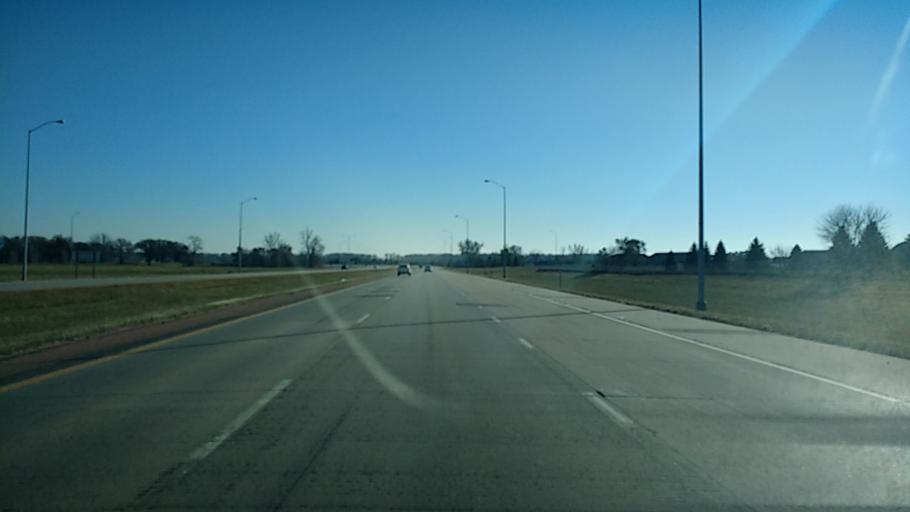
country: US
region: South Dakota
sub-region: Union County
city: Dakota Dunes
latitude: 42.5036
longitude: -96.4896
